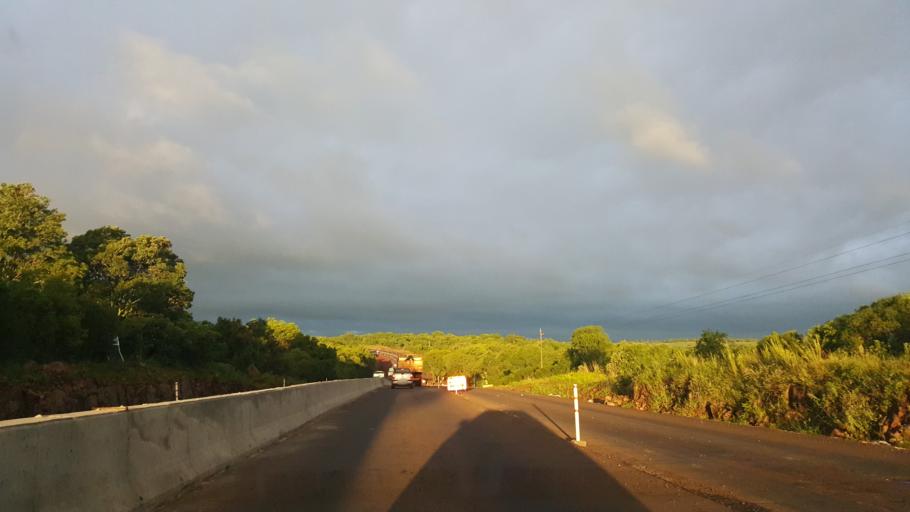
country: AR
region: Misiones
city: Santa Ana
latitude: -27.4239
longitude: -55.6208
